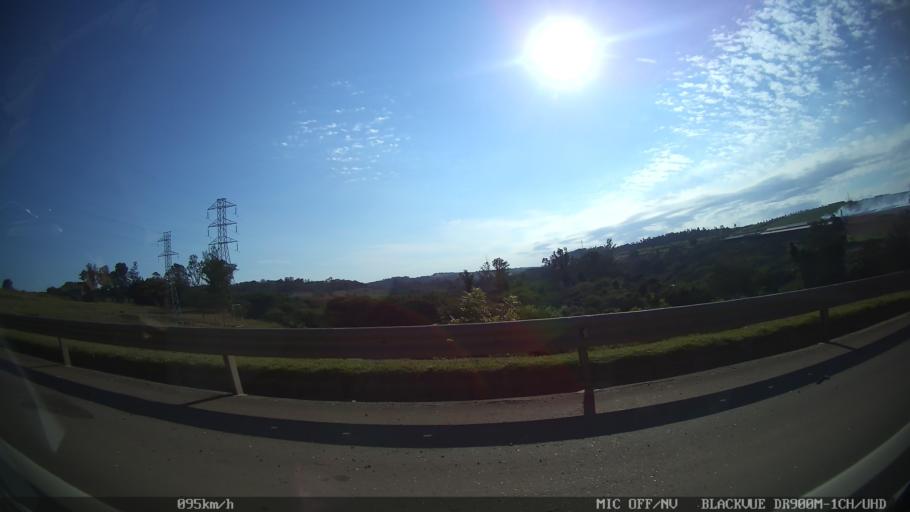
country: BR
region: Sao Paulo
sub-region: Piracicaba
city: Piracicaba
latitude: -22.7022
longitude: -47.6105
